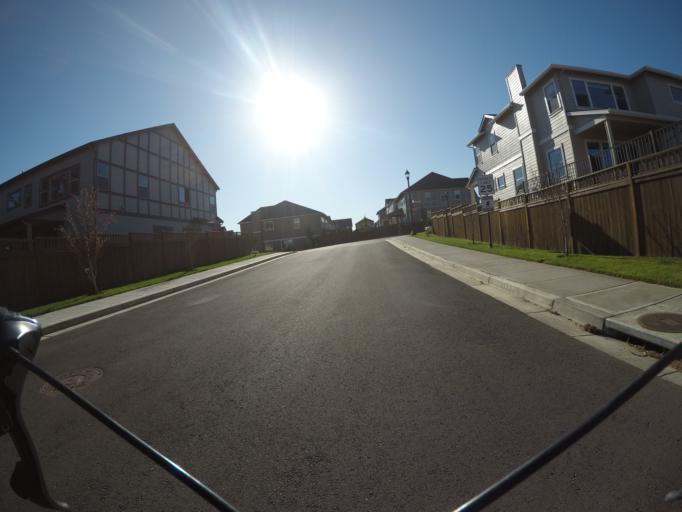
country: US
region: Oregon
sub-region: Washington County
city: King City
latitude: 45.4256
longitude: -122.8466
